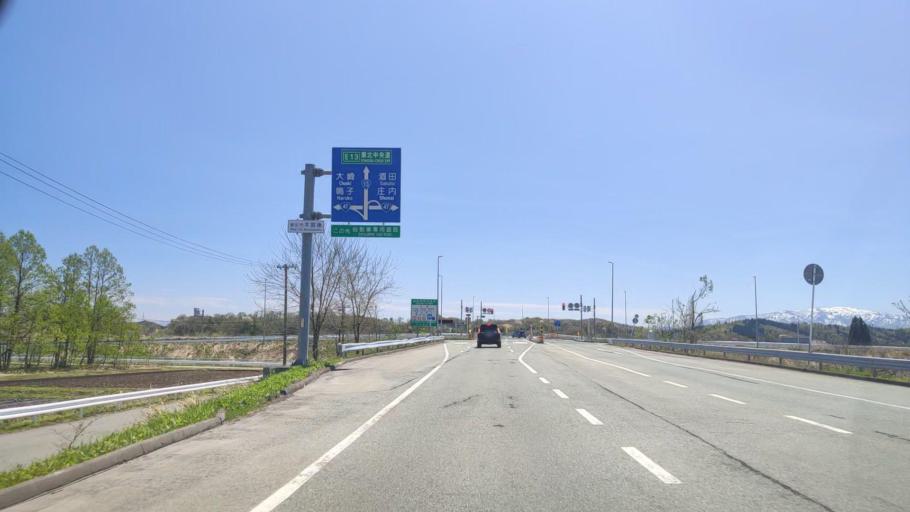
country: JP
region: Yamagata
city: Shinjo
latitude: 38.7428
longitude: 140.2948
